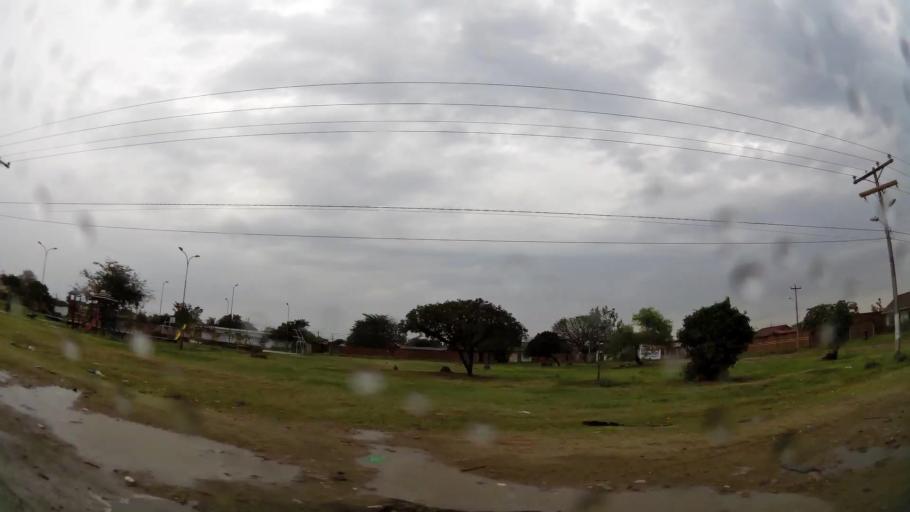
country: BO
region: Santa Cruz
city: Santa Cruz de la Sierra
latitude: -17.7581
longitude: -63.1299
